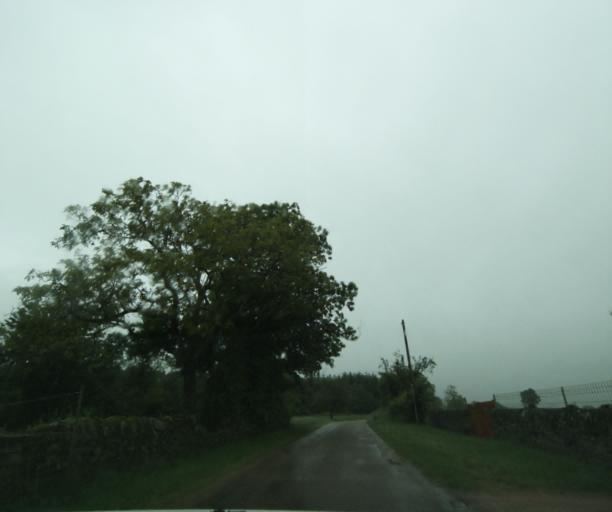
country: FR
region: Bourgogne
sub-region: Departement de Saone-et-Loire
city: Charolles
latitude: 46.3871
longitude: 4.3130
